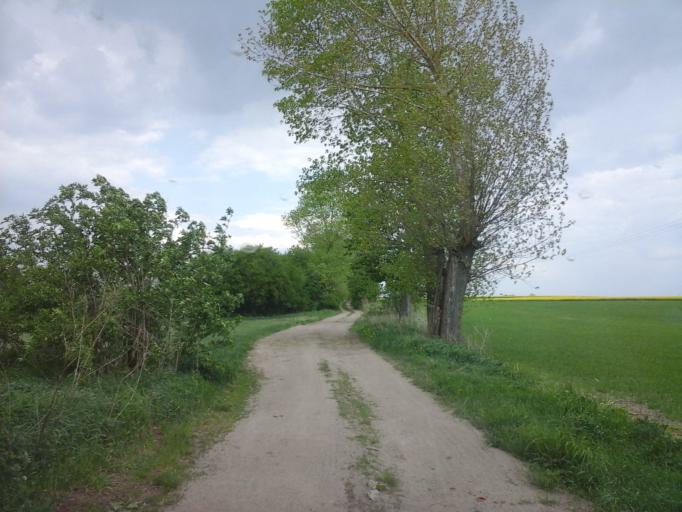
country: PL
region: West Pomeranian Voivodeship
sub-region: Powiat choszczenski
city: Choszczno
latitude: 53.1328
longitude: 15.3800
